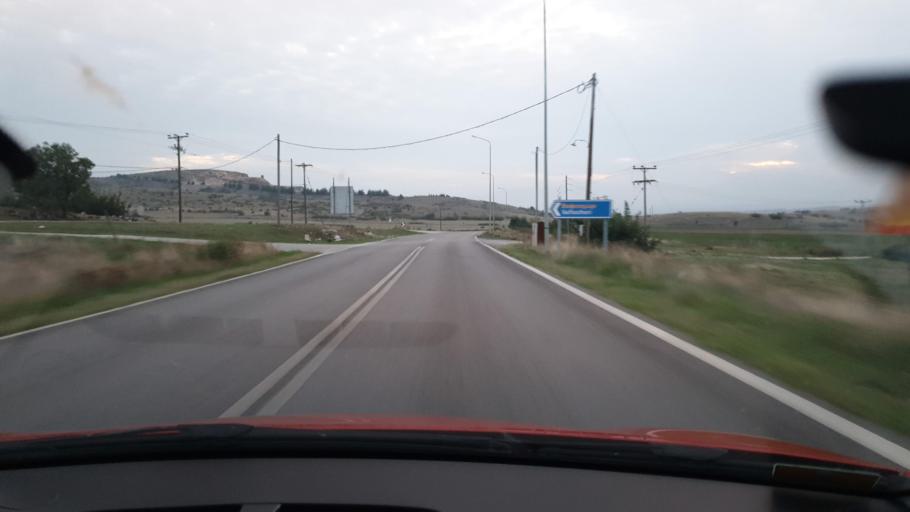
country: GR
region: Central Macedonia
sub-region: Nomos Kilkis
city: Polykastro
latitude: 41.0155
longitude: 22.6547
